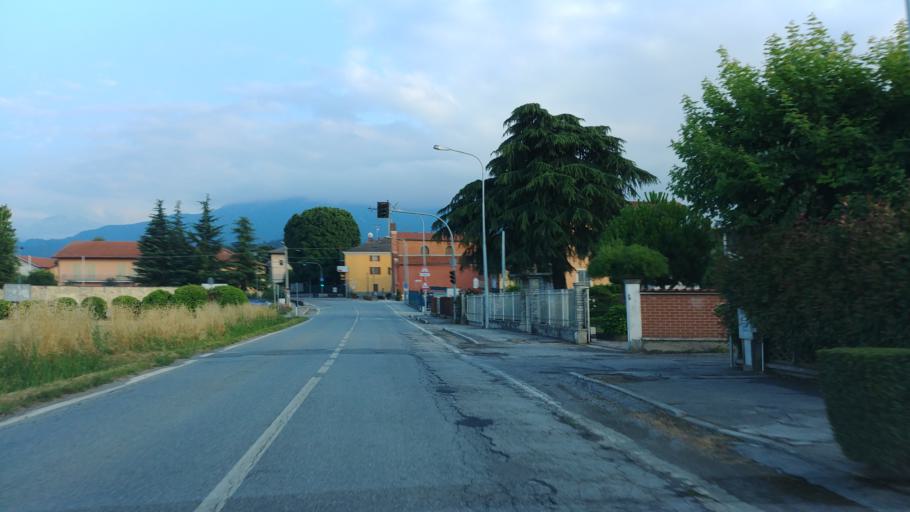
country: IT
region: Piedmont
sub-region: Provincia di Cuneo
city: Peveragno
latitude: 44.3483
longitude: 7.5933
